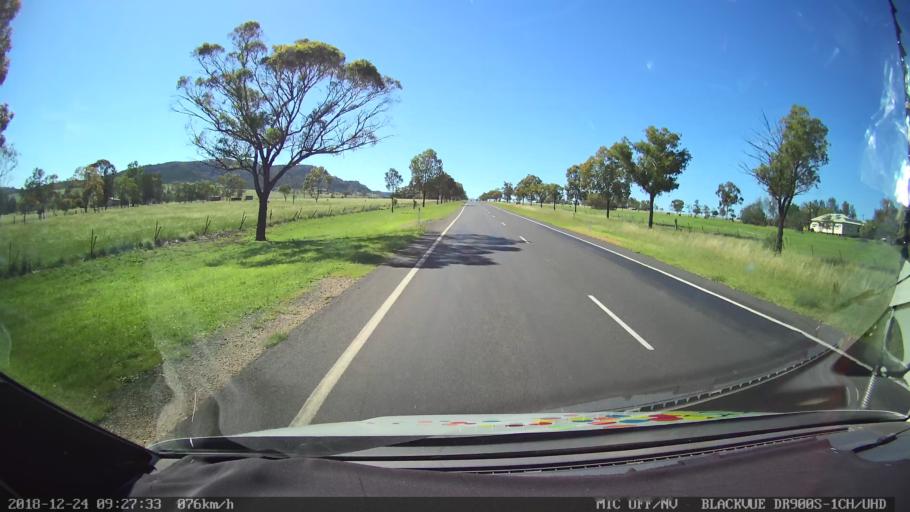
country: AU
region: New South Wales
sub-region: Liverpool Plains
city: Quirindi
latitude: -31.5291
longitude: 150.6819
